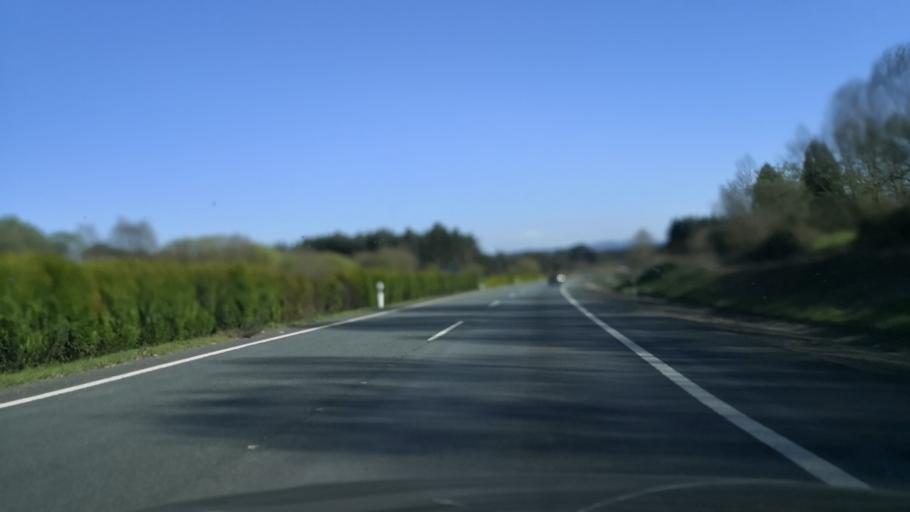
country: ES
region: Galicia
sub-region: Provincia da Coruna
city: Aranga
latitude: 43.2081
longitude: -8.0402
